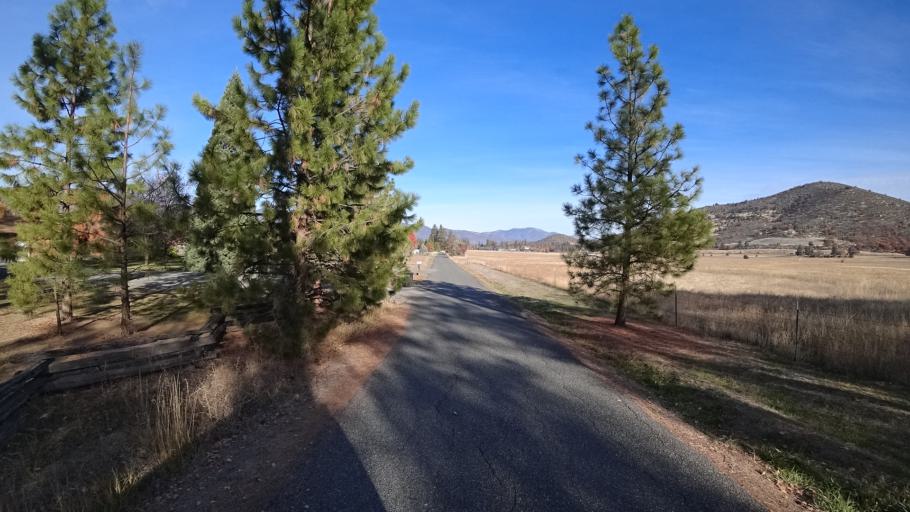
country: US
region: California
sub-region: Siskiyou County
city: Yreka
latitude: 41.6736
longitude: -122.6319
